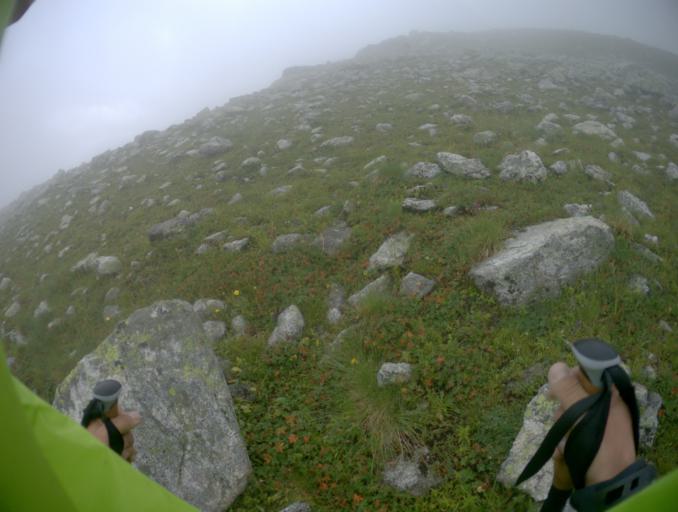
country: RU
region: Karachayevo-Cherkesiya
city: Uchkulan
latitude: 43.2854
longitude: 42.0985
